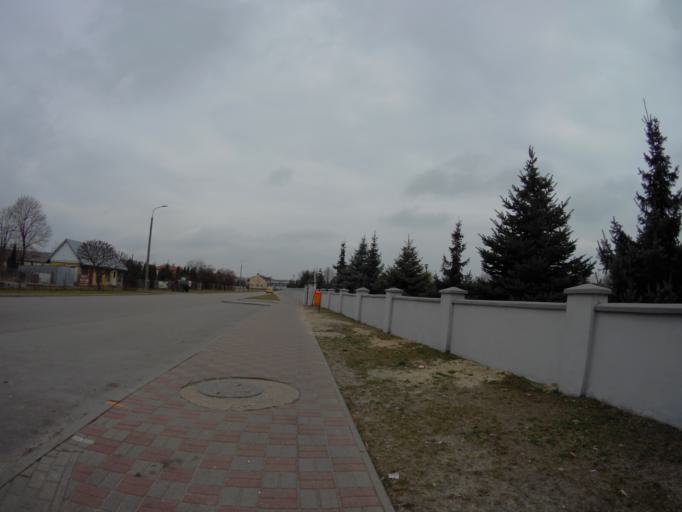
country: PL
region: Lublin Voivodeship
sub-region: Powiat bialski
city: Terespol
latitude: 52.0746
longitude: 23.6074
